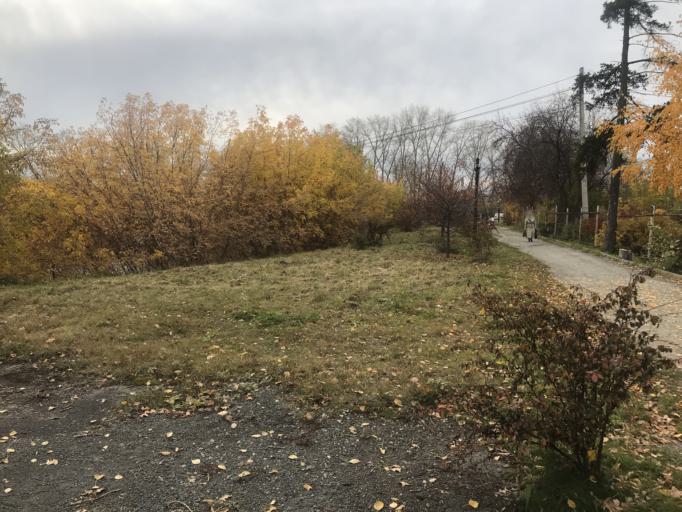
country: RU
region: Sverdlovsk
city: Aramil
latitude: 56.7001
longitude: 60.8317
